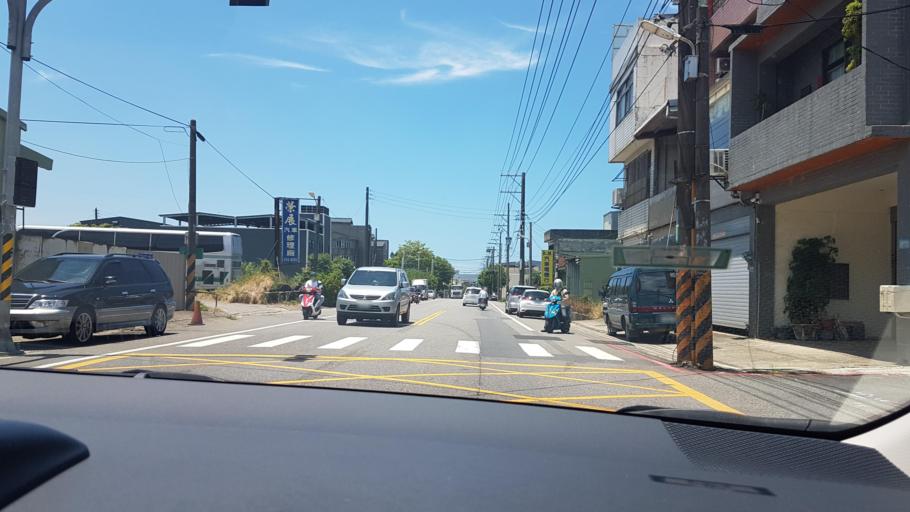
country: TW
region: Taiwan
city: Taoyuan City
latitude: 25.0874
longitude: 121.2808
